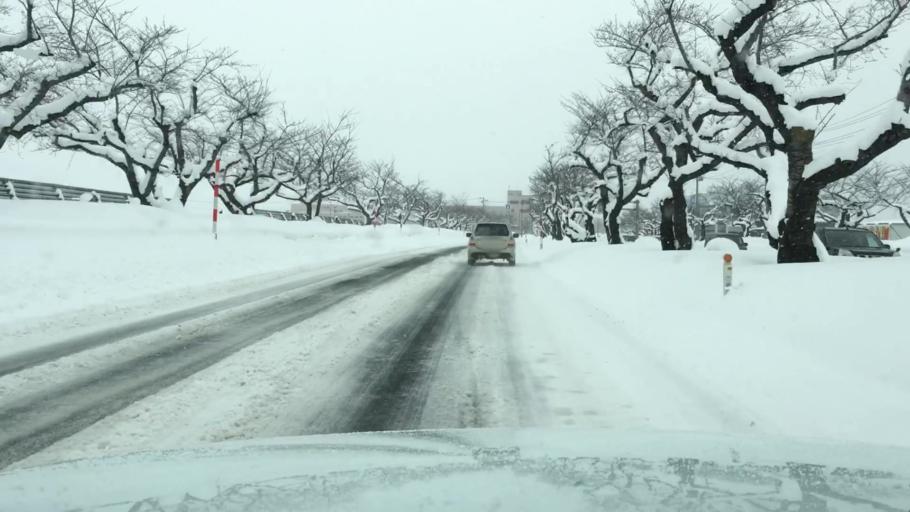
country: JP
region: Aomori
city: Hirosaki
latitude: 40.6382
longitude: 140.4890
